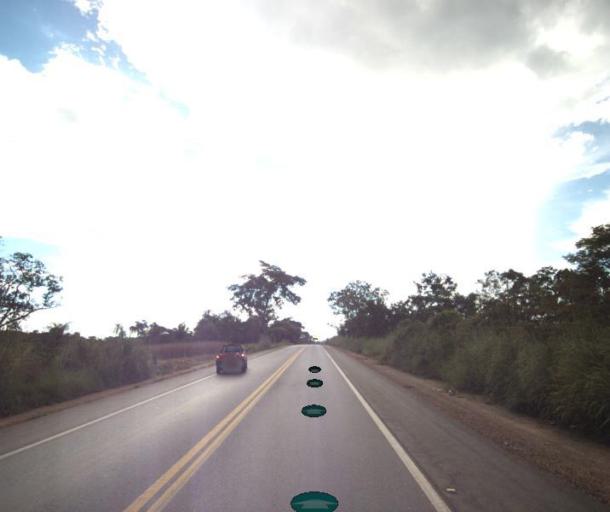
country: BR
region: Goias
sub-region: Jaragua
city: Jaragua
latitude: -15.6588
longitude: -49.3584
